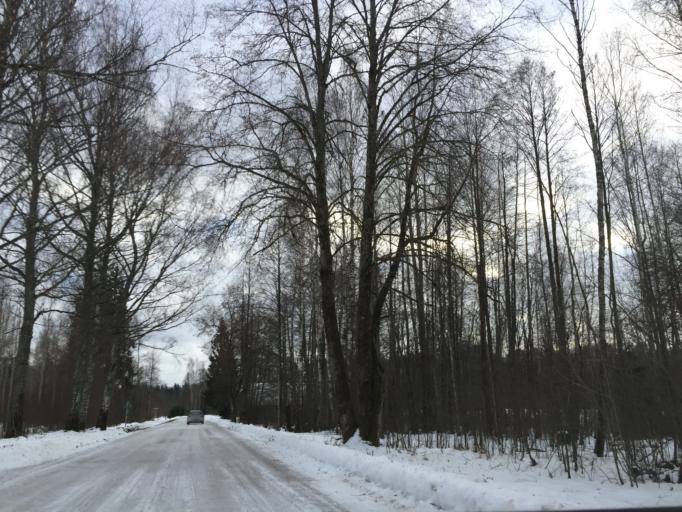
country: LV
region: Lielvarde
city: Lielvarde
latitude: 56.5792
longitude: 24.7882
